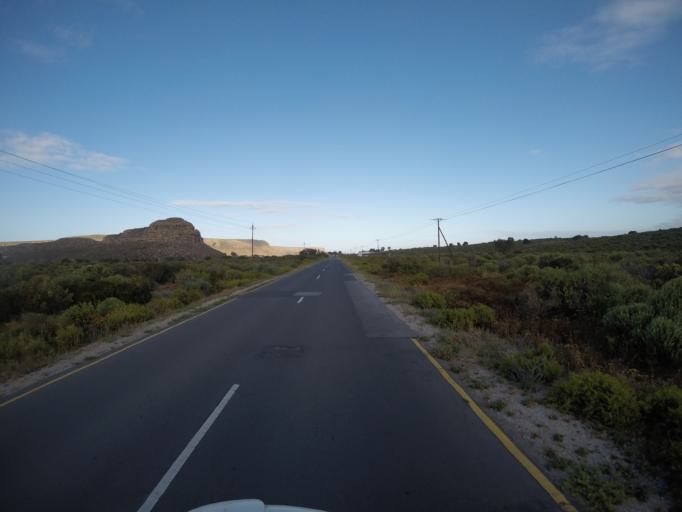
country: ZA
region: Western Cape
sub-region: West Coast District Municipality
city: Clanwilliam
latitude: -32.3129
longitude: 18.3628
